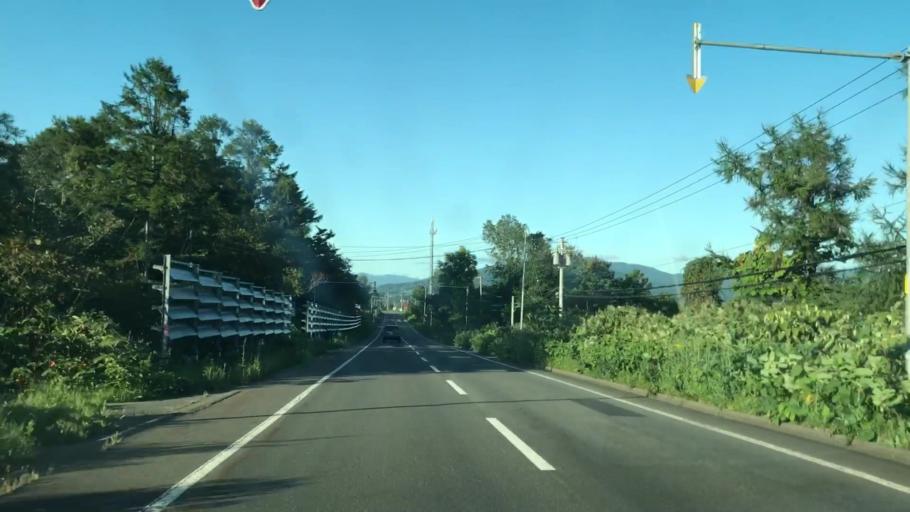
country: JP
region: Hokkaido
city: Date
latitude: 42.6229
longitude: 140.7956
